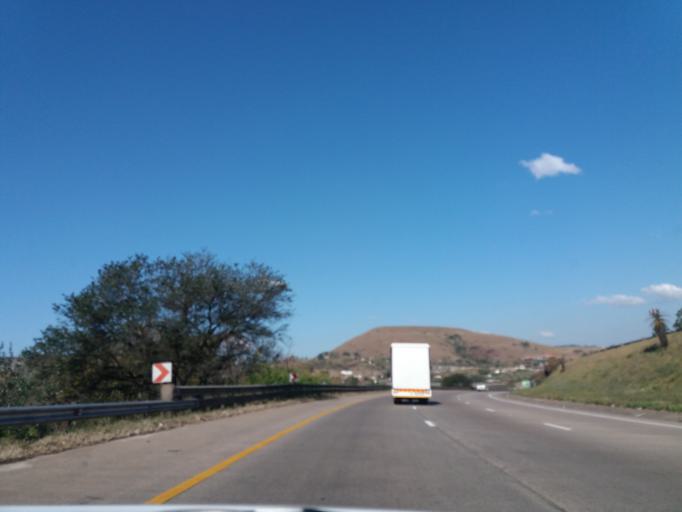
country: ZA
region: KwaZulu-Natal
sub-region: eThekwini Metropolitan Municipality
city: Mpumalanga
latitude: -29.7641
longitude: 30.6802
